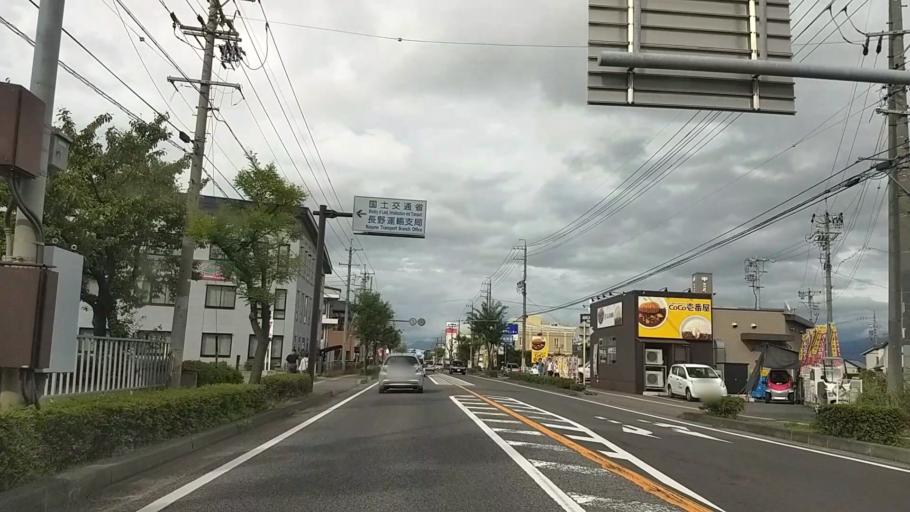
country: JP
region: Nagano
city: Nagano-shi
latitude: 36.6490
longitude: 138.2215
